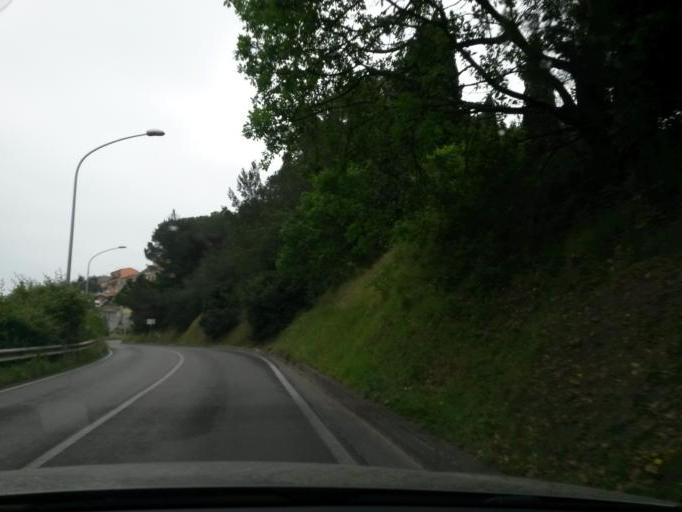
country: IT
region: Tuscany
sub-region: Provincia di Livorno
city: Capoliveri
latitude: 42.7463
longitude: 10.3733
